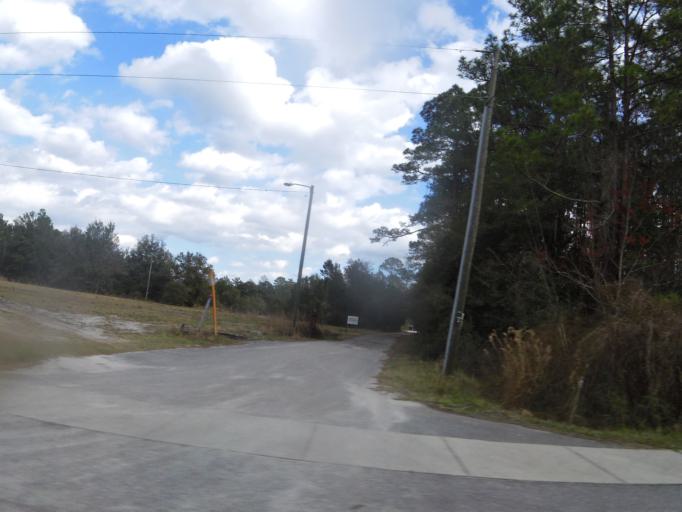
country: US
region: Florida
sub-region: Volusia County
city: Pierson
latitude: 29.2300
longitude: -81.4623
